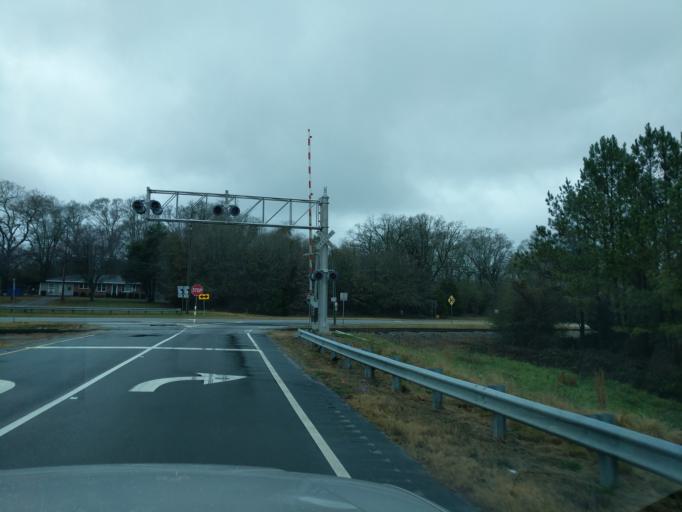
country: US
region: Georgia
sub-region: Hart County
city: Royston
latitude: 34.2997
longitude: -83.1060
